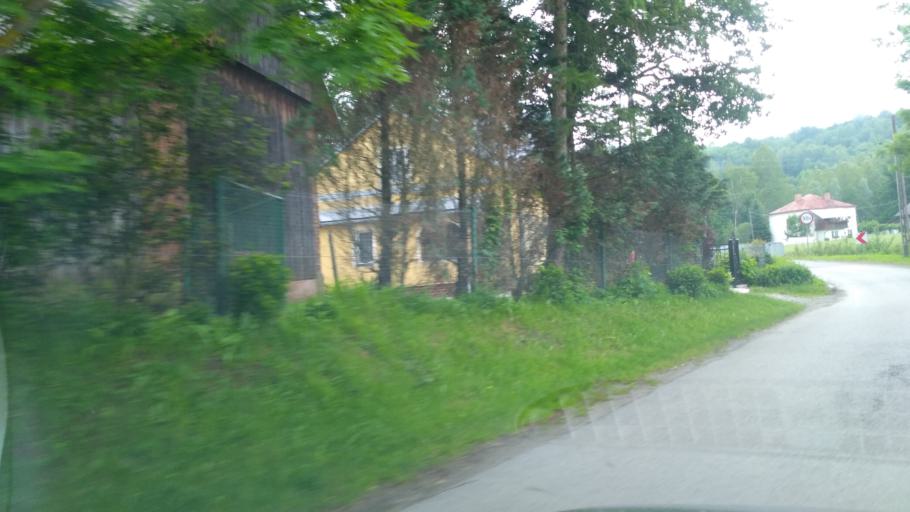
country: PL
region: Subcarpathian Voivodeship
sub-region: Powiat przemyski
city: Nienadowa
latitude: 49.8445
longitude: 22.4135
